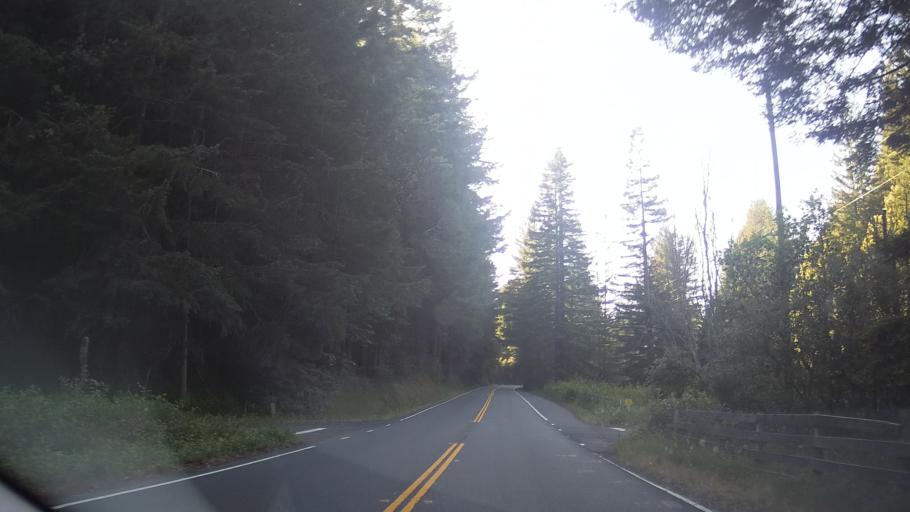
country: US
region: California
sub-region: Mendocino County
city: Fort Bragg
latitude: 39.3497
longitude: -123.6039
